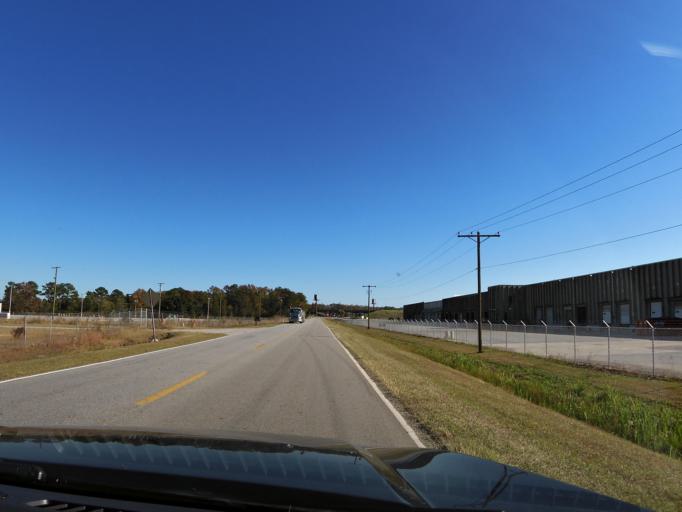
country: US
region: Georgia
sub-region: Chatham County
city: Savannah
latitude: 32.0681
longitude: -81.1417
